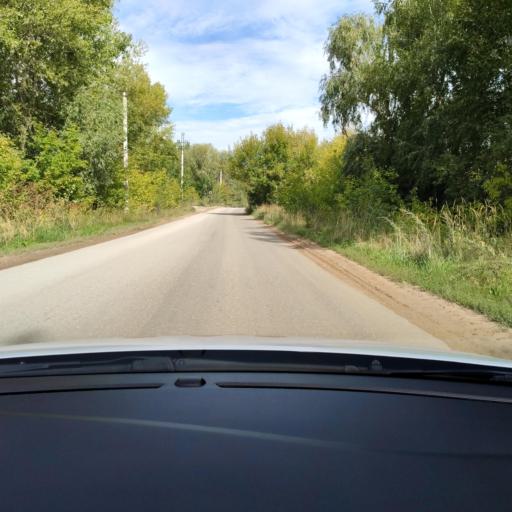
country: RU
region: Tatarstan
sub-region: Gorod Kazan'
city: Kazan
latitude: 55.7235
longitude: 49.0950
